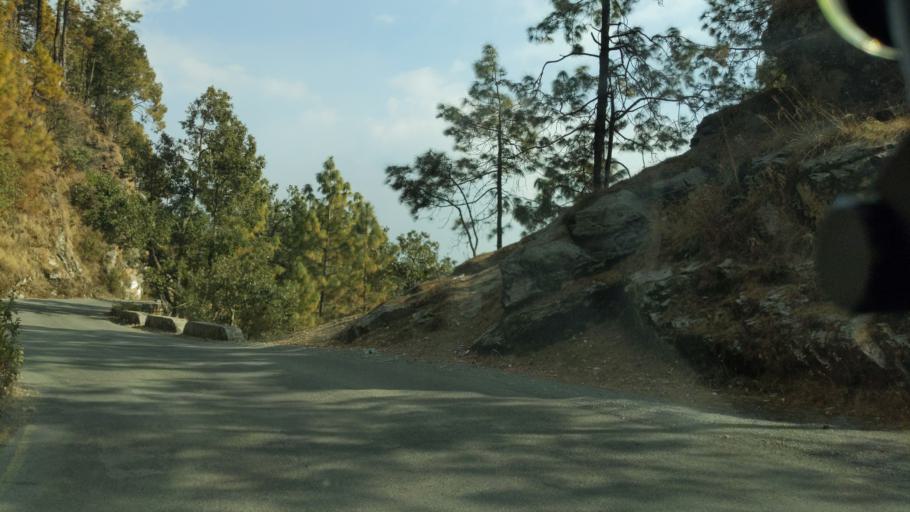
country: IN
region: Uttarakhand
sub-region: Naini Tal
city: Bhowali
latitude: 29.4024
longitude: 79.5357
